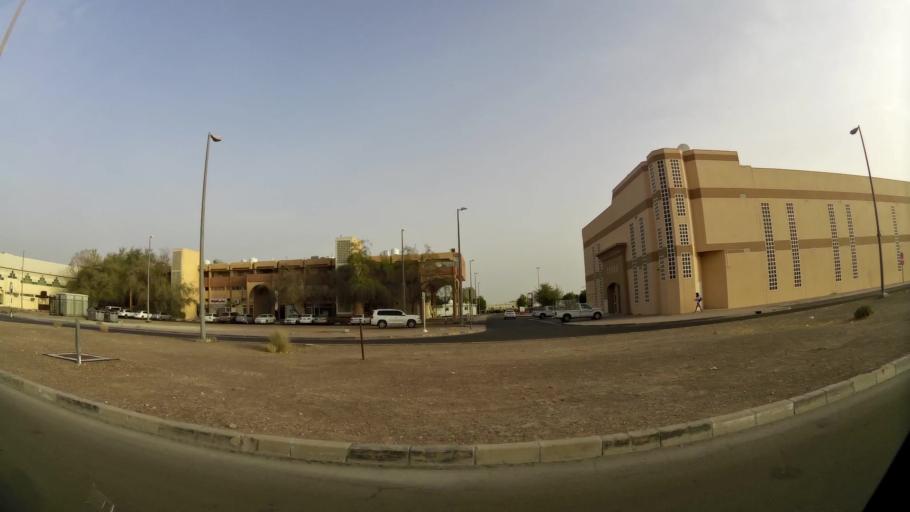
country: OM
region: Al Buraimi
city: Al Buraymi
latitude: 24.2426
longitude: 55.7453
